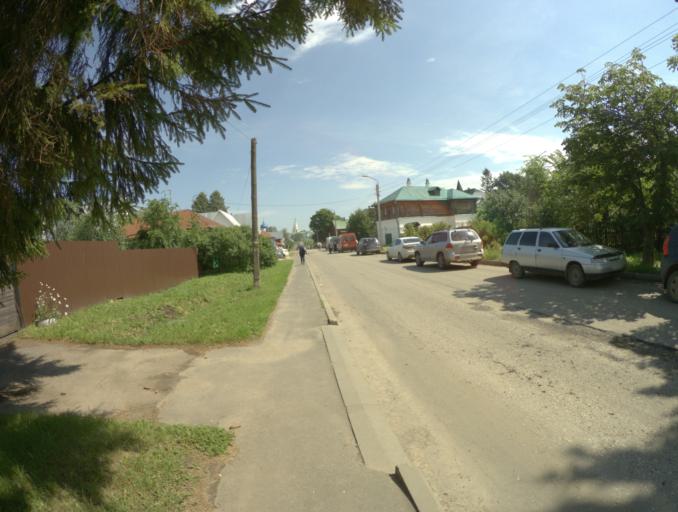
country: RU
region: Vladimir
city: Suzdal'
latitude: 56.4133
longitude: 40.4356
